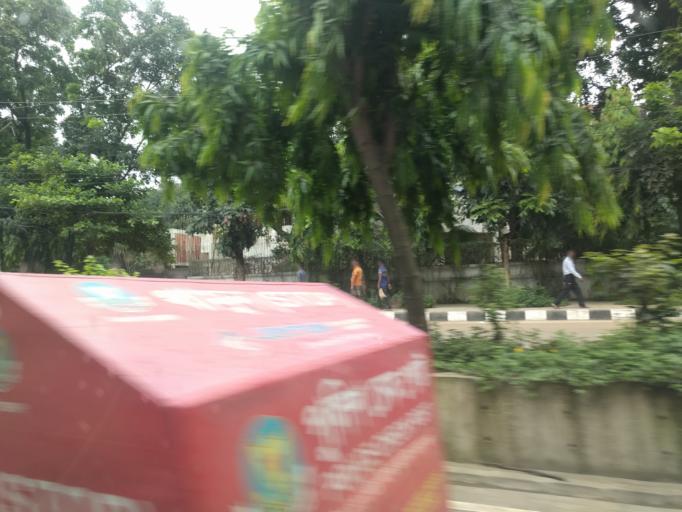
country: BD
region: Dhaka
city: Paltan
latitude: 23.7962
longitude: 90.4135
